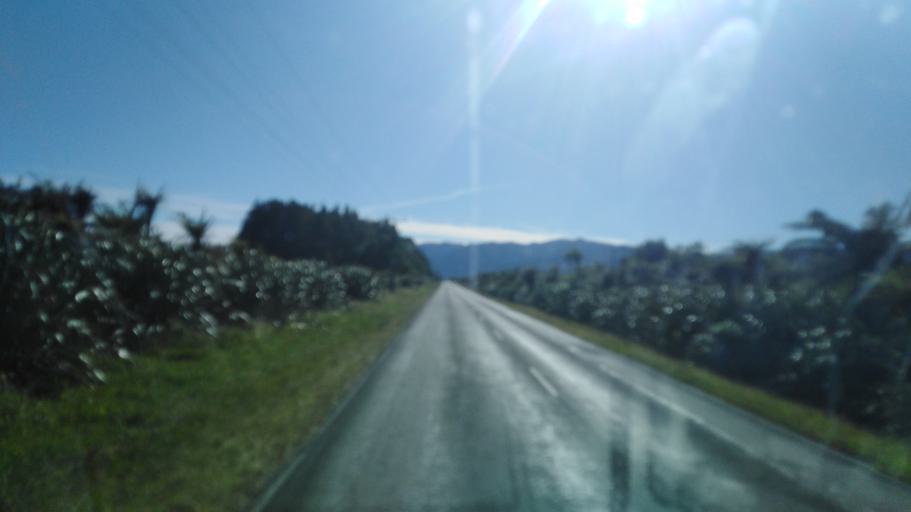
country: NZ
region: West Coast
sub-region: Buller District
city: Westport
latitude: -41.7426
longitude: 171.6919
